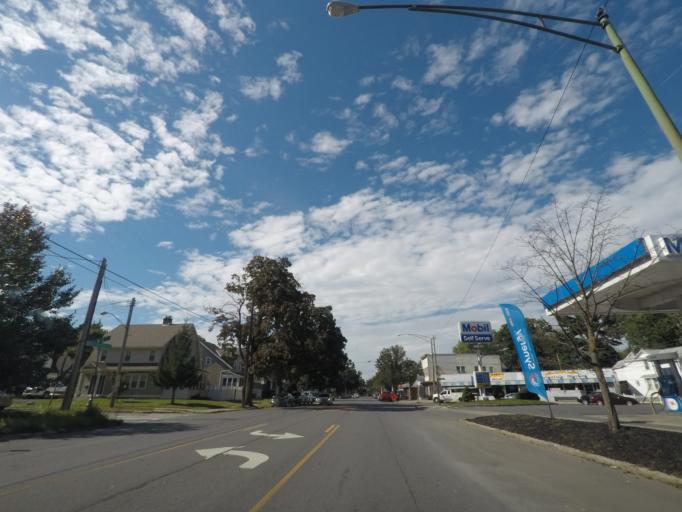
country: US
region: New York
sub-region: Albany County
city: Albany
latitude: 42.6530
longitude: -73.7858
